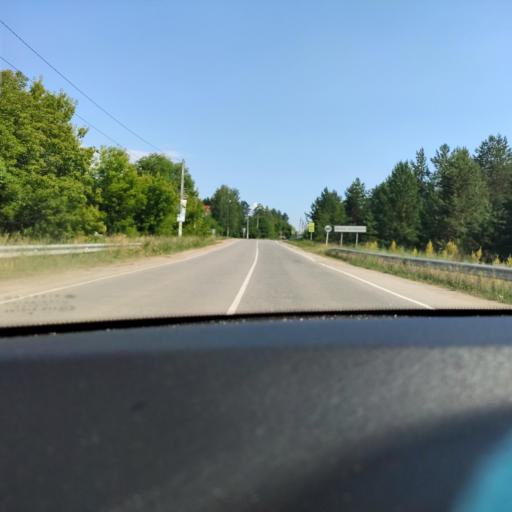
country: RU
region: Samara
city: Volzhskiy
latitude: 53.4537
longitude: 50.1695
